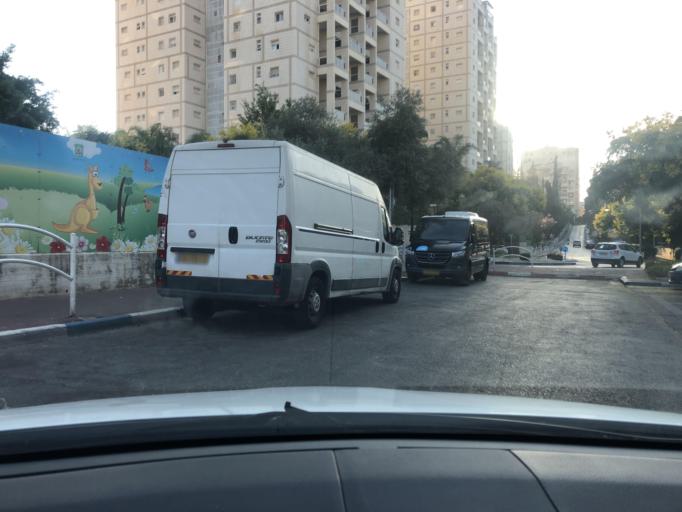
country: IL
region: Tel Aviv
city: Bene Beraq
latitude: 32.0736
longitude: 34.8317
